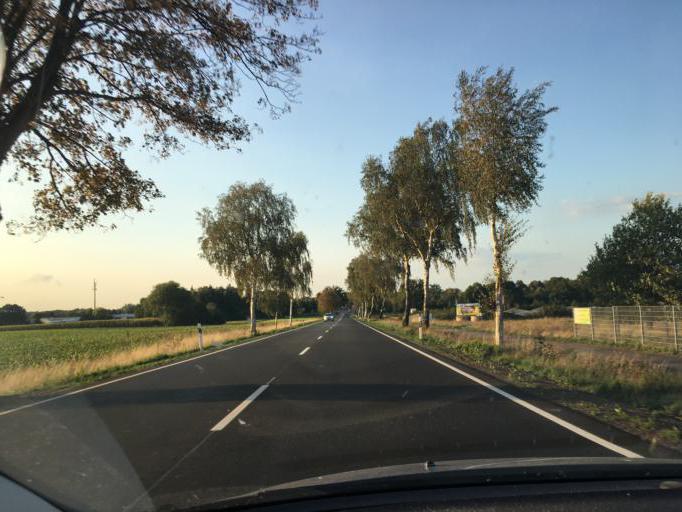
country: DE
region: Lower Saxony
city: Bergen
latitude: 52.7959
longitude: 9.9704
